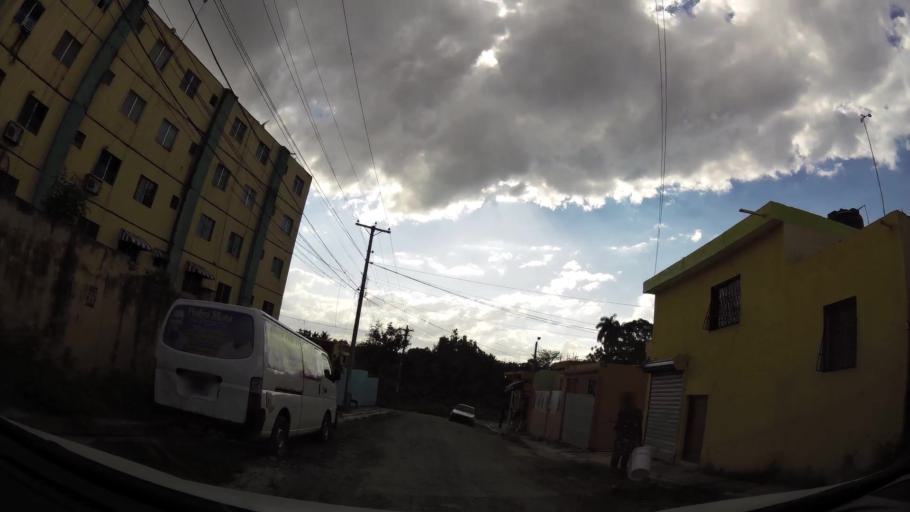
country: DO
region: Nacional
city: Ensanche Luperon
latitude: 18.5627
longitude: -69.9109
